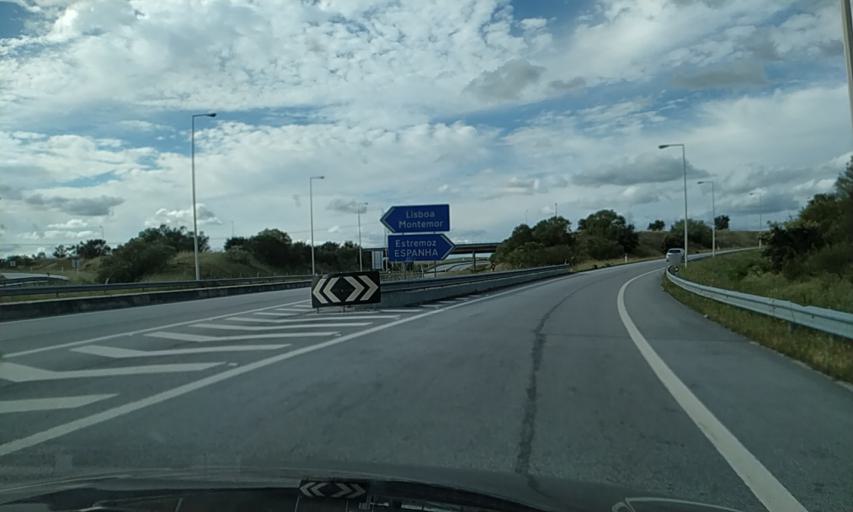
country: PT
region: Evora
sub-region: Evora
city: Evora
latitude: 38.6450
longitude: -7.8561
